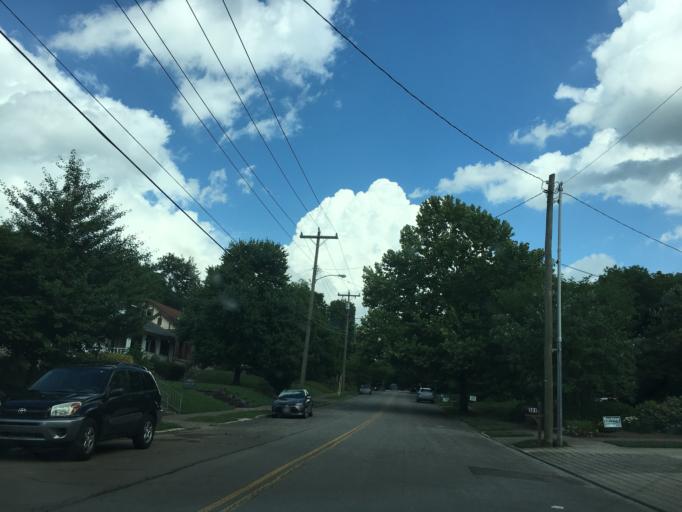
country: US
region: Tennessee
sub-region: Davidson County
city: Nashville
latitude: 36.1363
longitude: -86.8190
